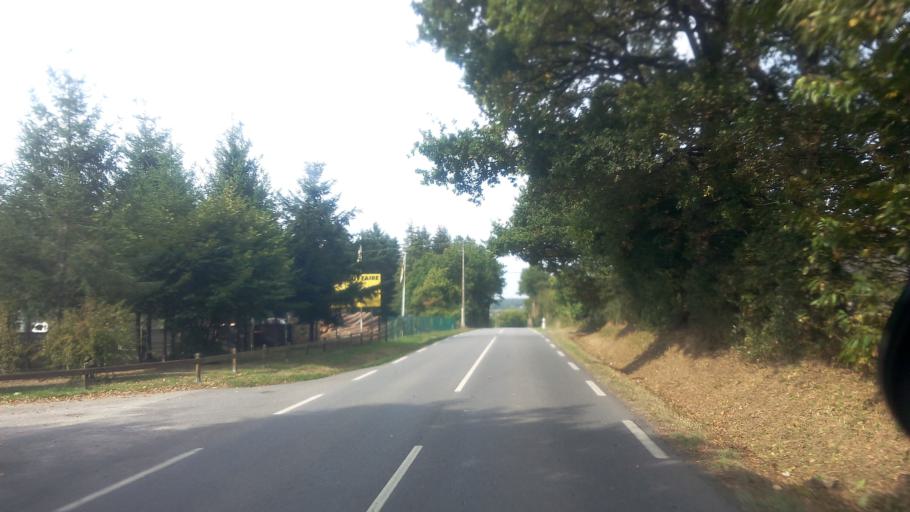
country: FR
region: Brittany
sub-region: Departement d'Ille-et-Vilaine
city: Bains-sur-Oust
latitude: 47.7241
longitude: -2.1022
